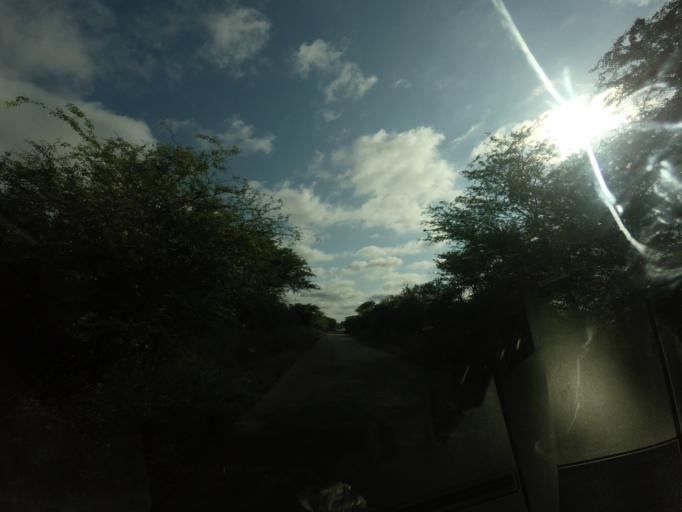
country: ZA
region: Mpumalanga
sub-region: Ehlanzeni District
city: Komatipoort
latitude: -25.2113
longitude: 31.8708
